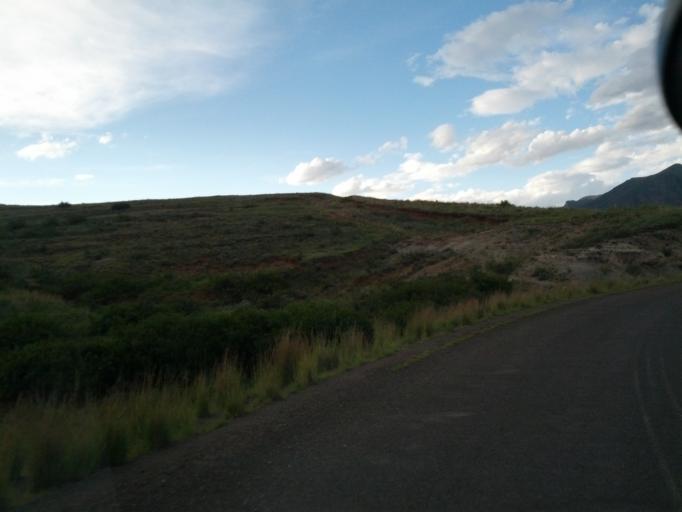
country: LS
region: Qacha's Nek
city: Qacha's Nek
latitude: -30.0763
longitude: 28.5795
